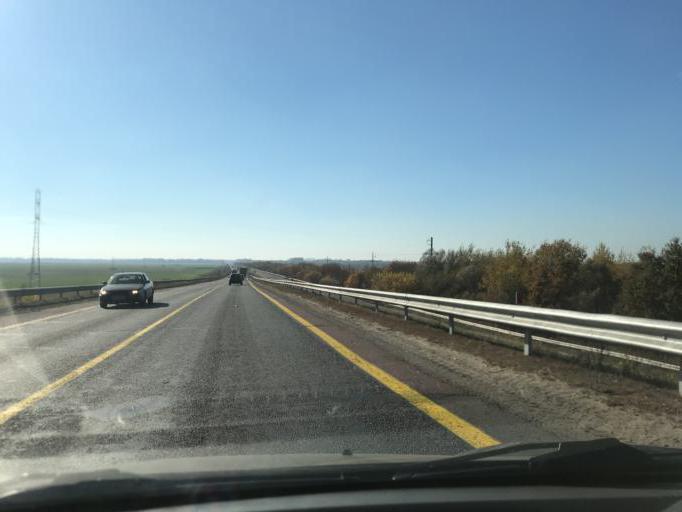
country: BY
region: Gomel
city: Horad Rechytsa
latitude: 52.3209
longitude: 30.5231
